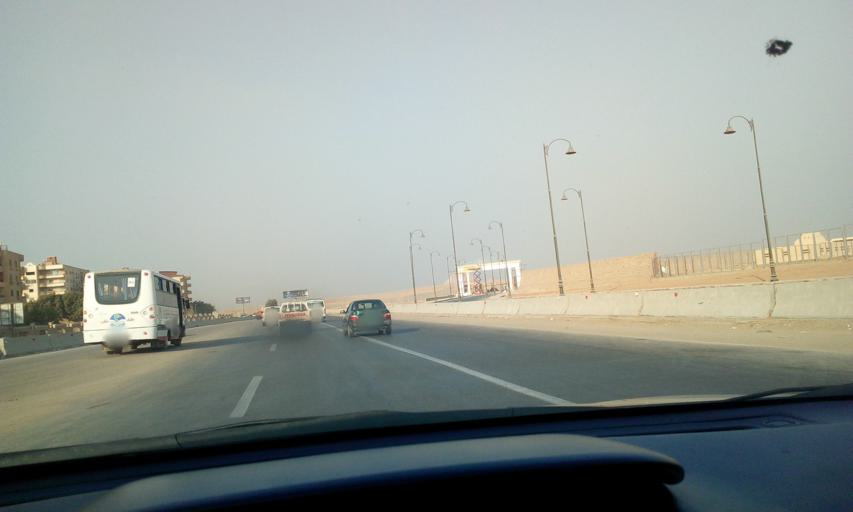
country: EG
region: Al Jizah
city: Al Jizah
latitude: 29.9558
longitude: 31.1060
